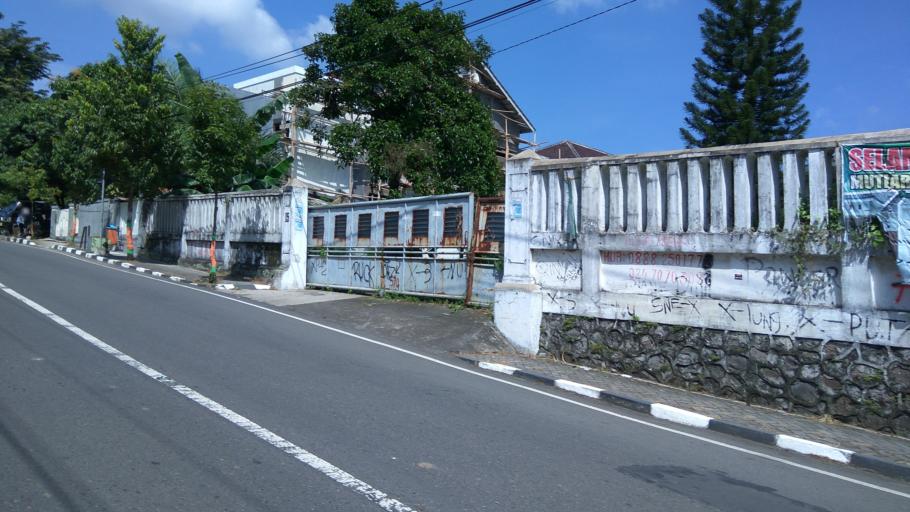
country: ID
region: Central Java
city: Ungaran
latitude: -7.1375
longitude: 110.4071
